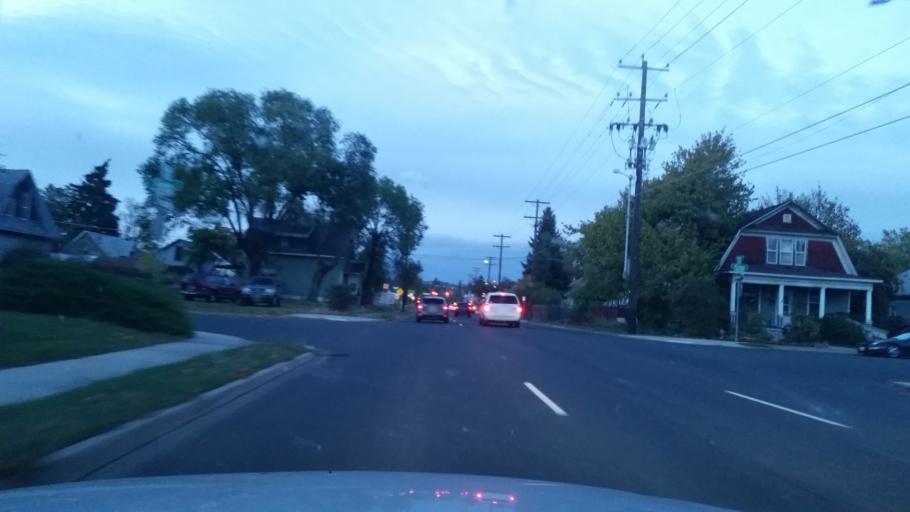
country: US
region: Washington
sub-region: Spokane County
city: Spokane
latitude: 47.6765
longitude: -117.4356
